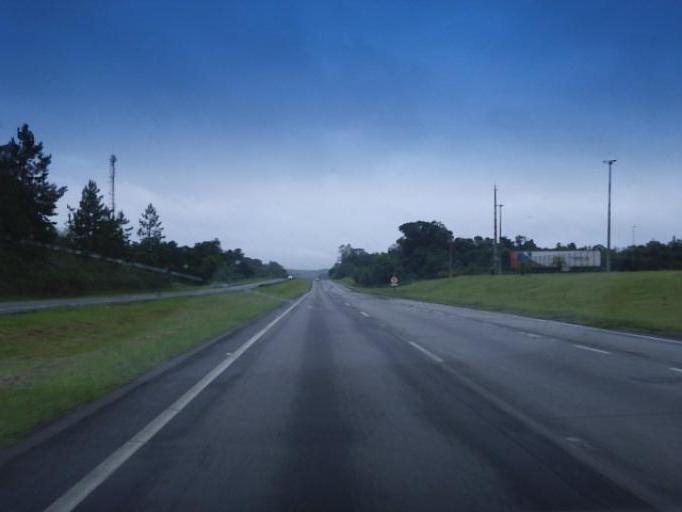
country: BR
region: Sao Paulo
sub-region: Registro
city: Registro
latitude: -24.4447
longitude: -47.8019
